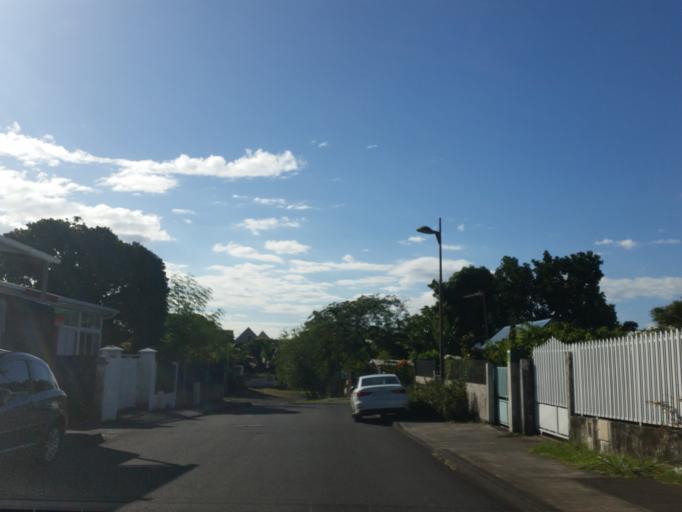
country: RE
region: Reunion
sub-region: Reunion
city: Saint-Andre
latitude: -20.9694
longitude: 55.6587
